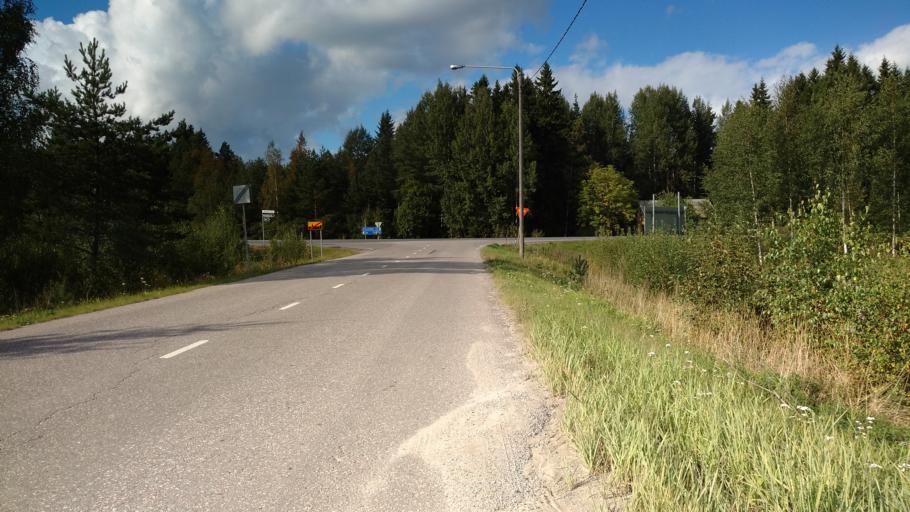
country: FI
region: Varsinais-Suomi
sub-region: Salo
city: Salo
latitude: 60.3815
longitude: 23.1911
